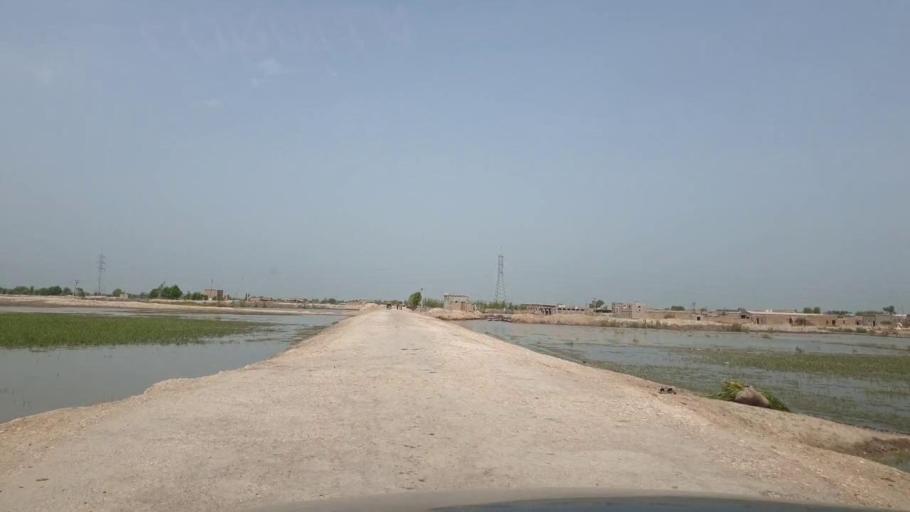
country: PK
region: Sindh
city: Garhi Yasin
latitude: 27.8545
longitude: 68.4289
